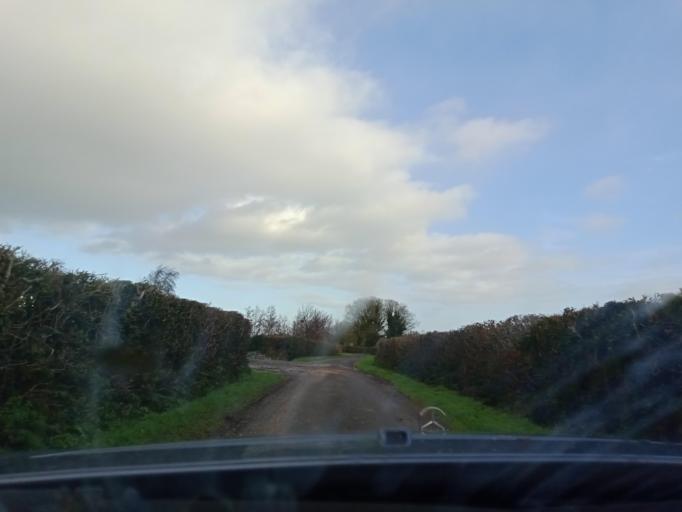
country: IE
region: Leinster
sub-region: Kilkenny
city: Callan
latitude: 52.4833
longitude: -7.3683
